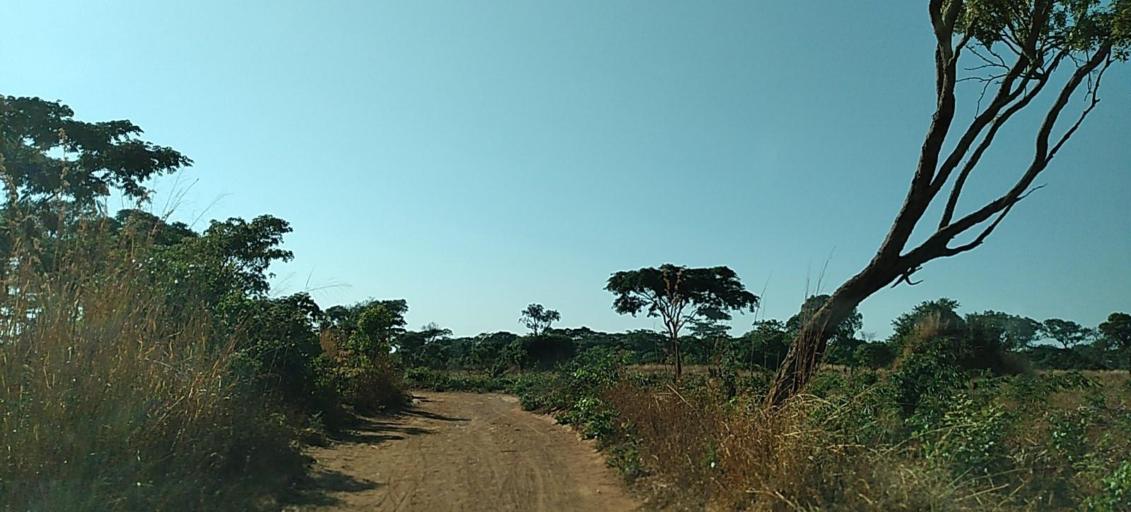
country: ZM
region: Copperbelt
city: Chililabombwe
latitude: -12.3703
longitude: 27.9022
